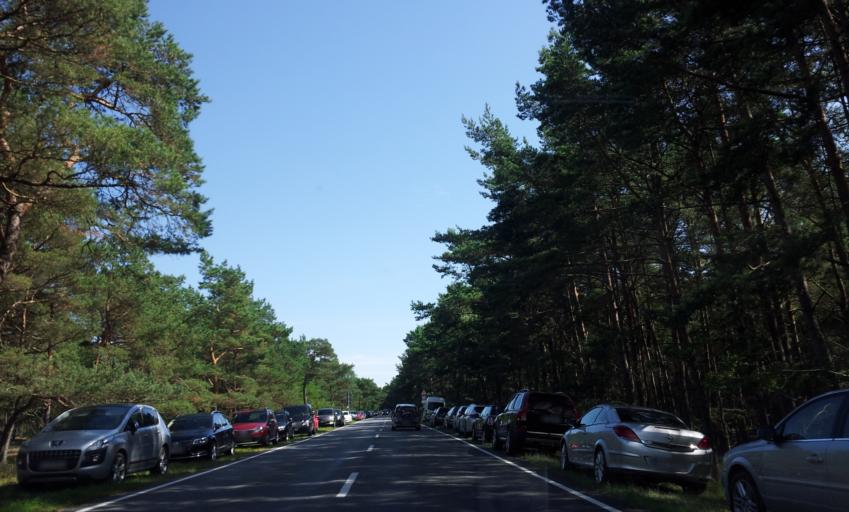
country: DE
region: Mecklenburg-Vorpommern
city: Glowe
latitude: 54.5820
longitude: 13.4071
